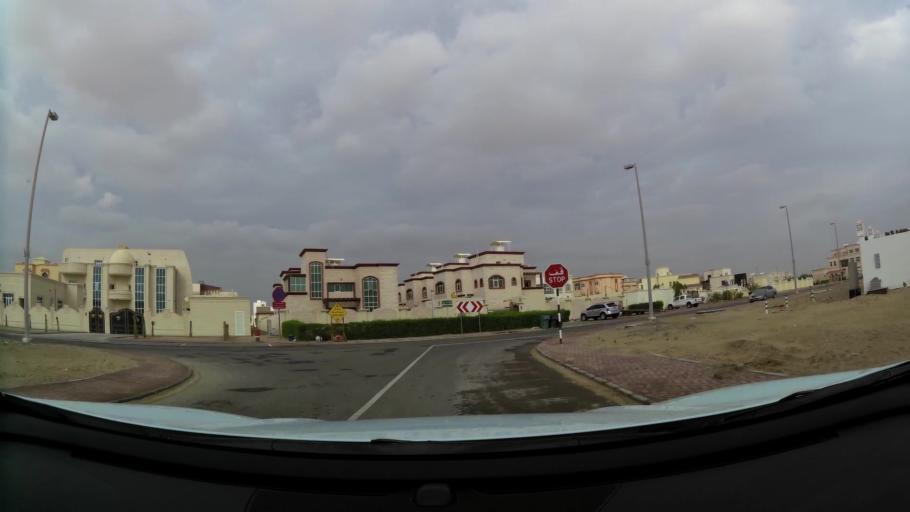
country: AE
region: Abu Dhabi
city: Abu Dhabi
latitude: 24.3425
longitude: 54.6264
